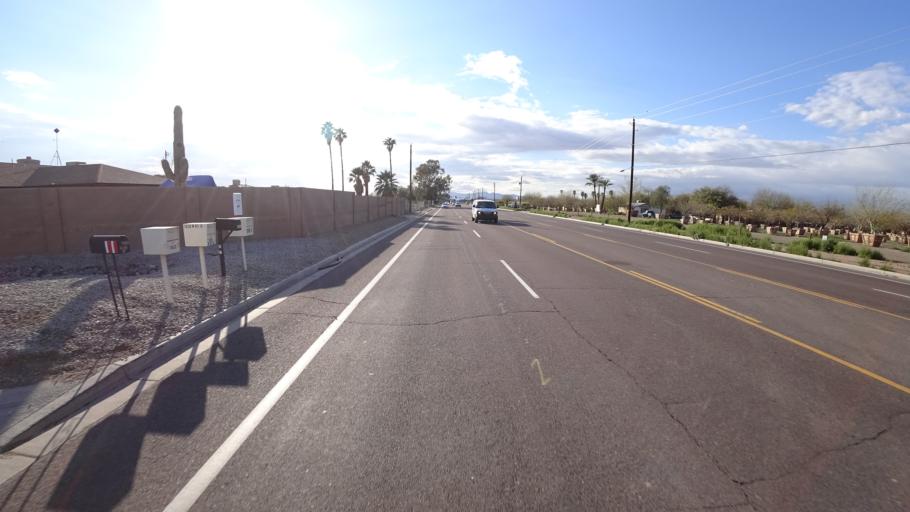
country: US
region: Arizona
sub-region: Maricopa County
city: Peoria
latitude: 33.5520
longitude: -112.2344
